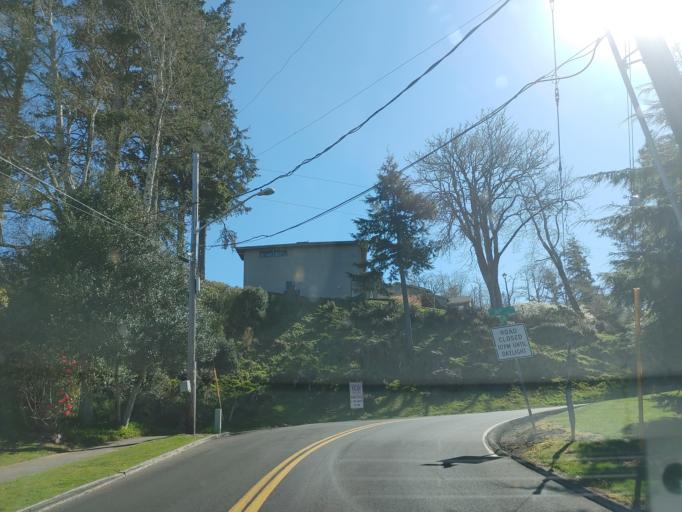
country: US
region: Oregon
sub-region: Clatsop County
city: Astoria
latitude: 46.1822
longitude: -123.8254
